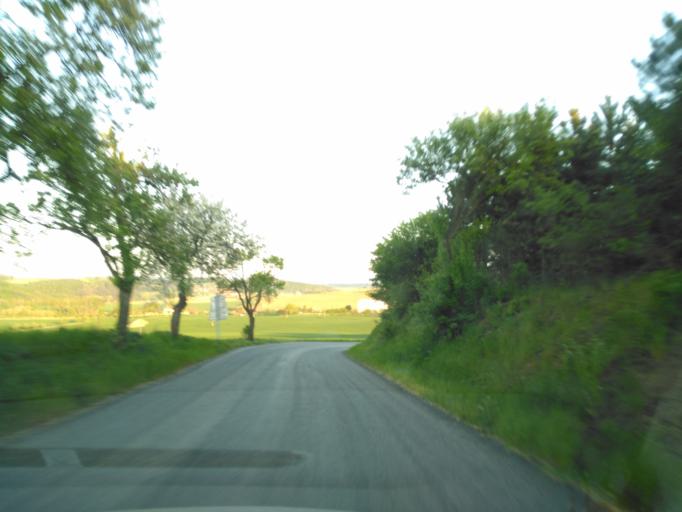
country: CZ
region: Central Bohemia
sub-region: Okres Beroun
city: Kraluv Dvur
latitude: 49.9129
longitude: 14.0336
